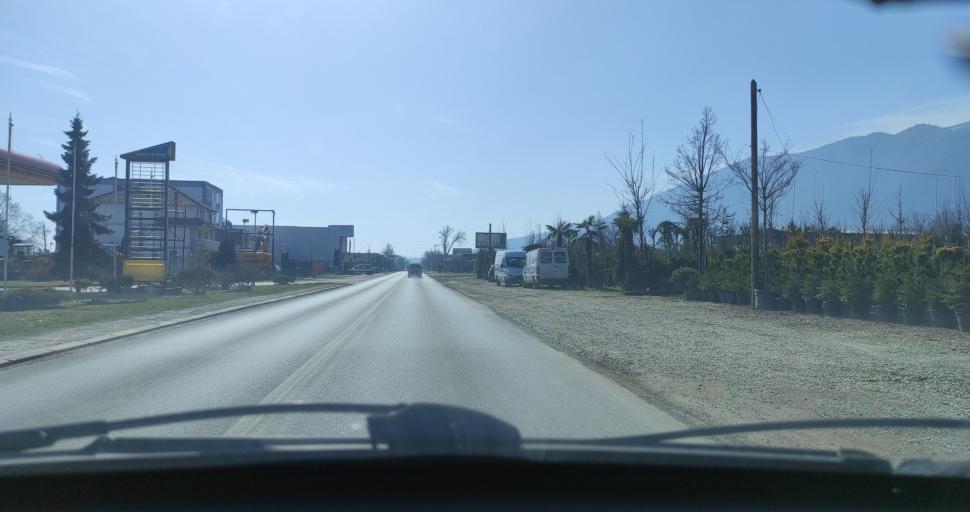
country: XK
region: Pec
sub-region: Komuna e Pejes
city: Peje
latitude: 42.6251
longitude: 20.3052
